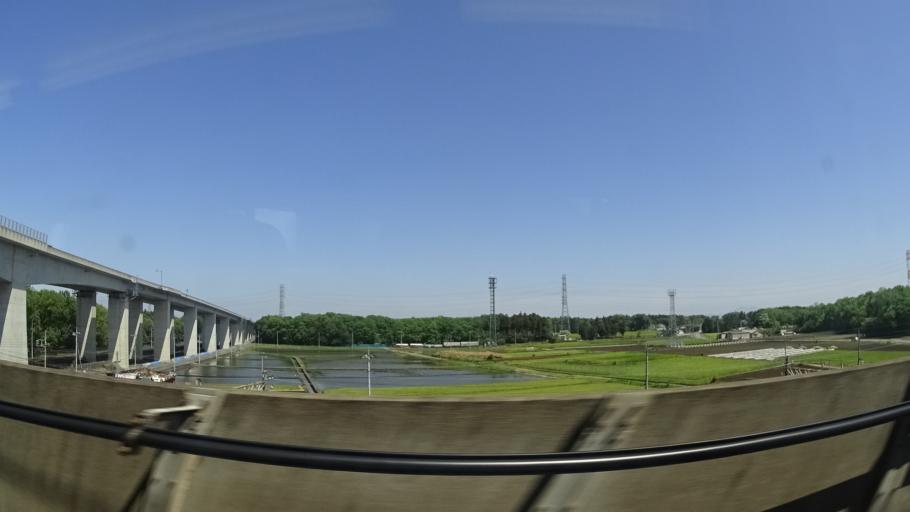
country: JP
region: Tochigi
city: Kaminokawa
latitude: 36.4639
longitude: 139.8717
